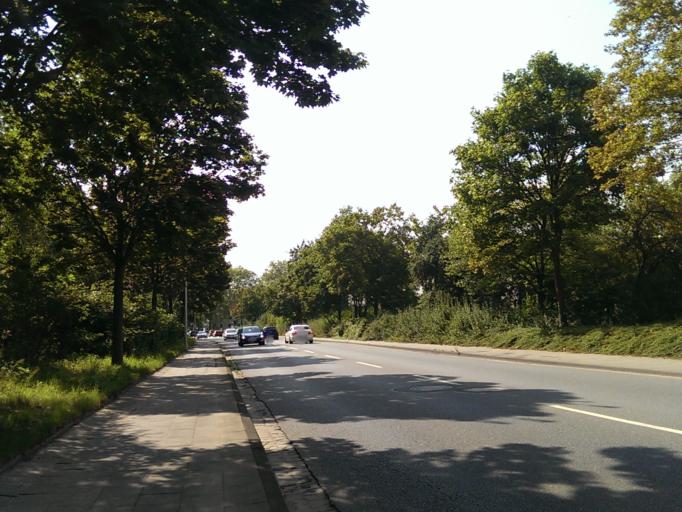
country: DE
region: Lower Saxony
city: Hildesheim
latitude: 52.1744
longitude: 9.9553
